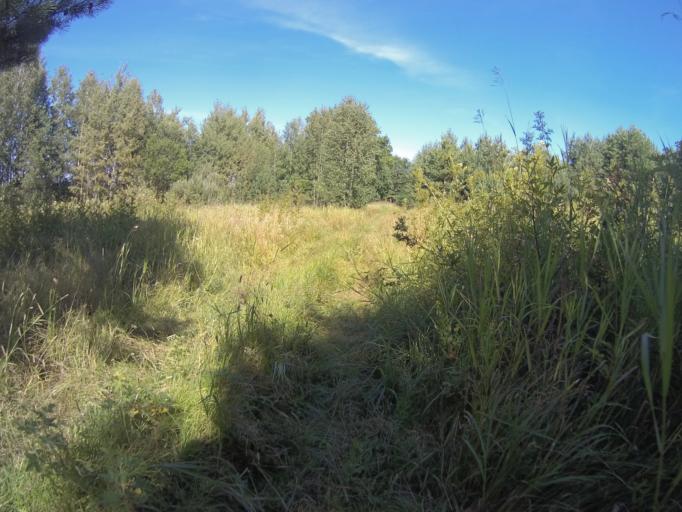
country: RU
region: Vladimir
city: Raduzhnyy
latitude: 56.0293
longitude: 40.2590
